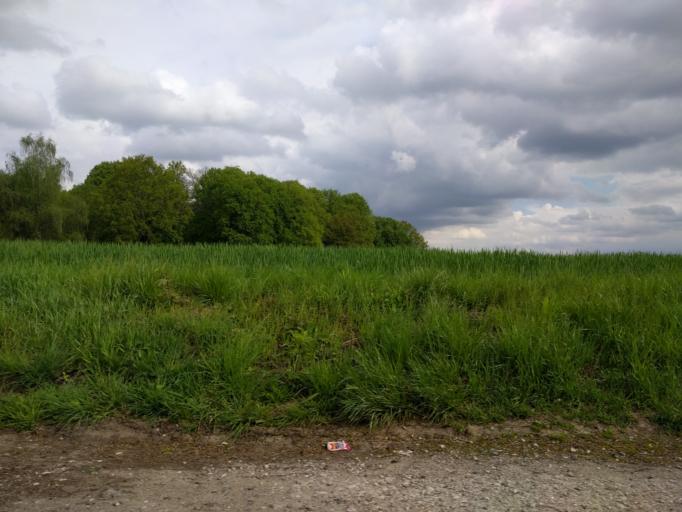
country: DE
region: North Rhine-Westphalia
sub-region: Regierungsbezirk Detmold
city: Bielefeld
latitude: 52.0500
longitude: 8.5842
